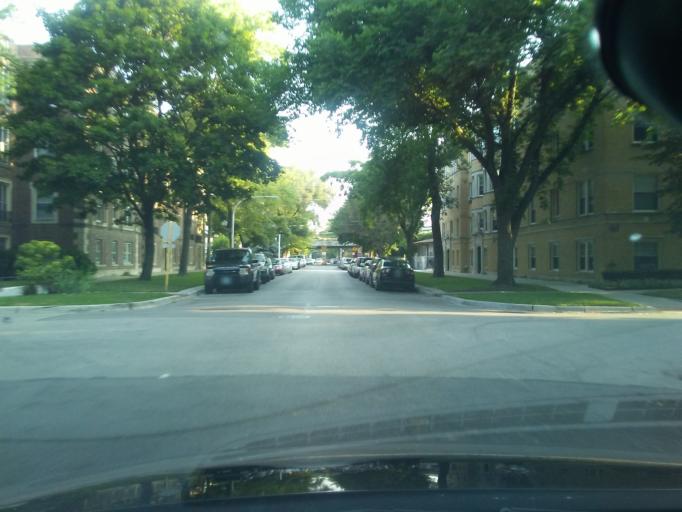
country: US
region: Illinois
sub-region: Cook County
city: Evanston
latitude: 42.0138
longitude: -87.6680
